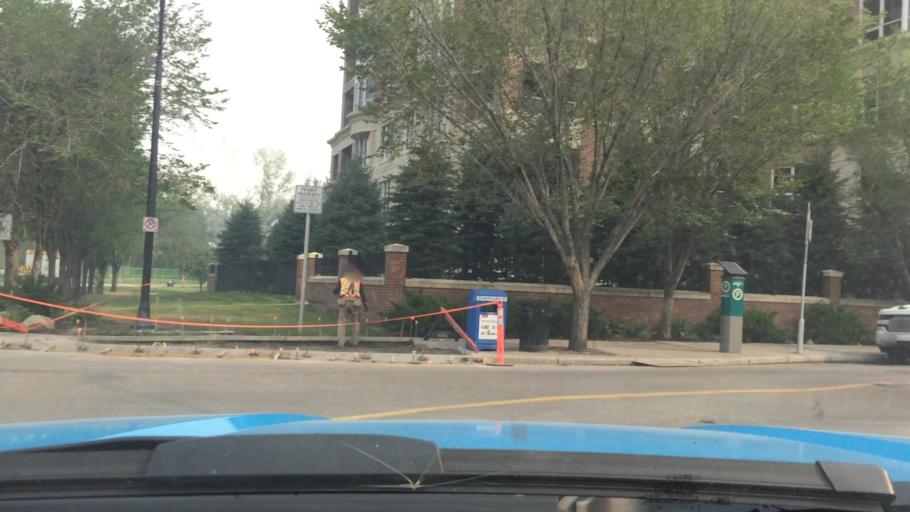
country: CA
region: Alberta
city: Calgary
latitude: 51.0525
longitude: -114.0758
